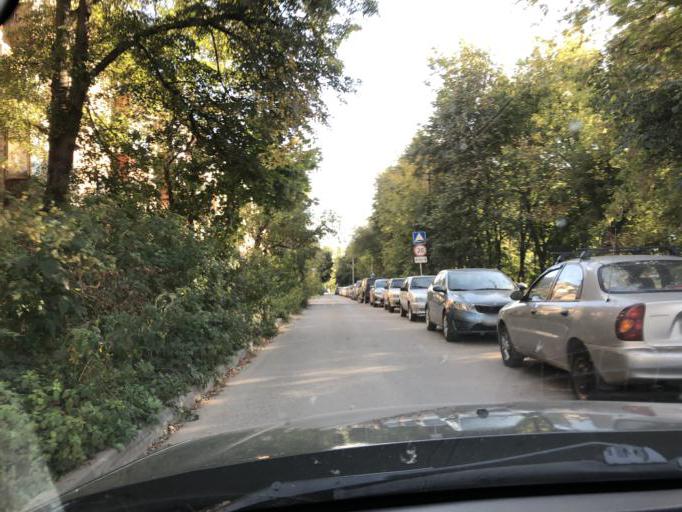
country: RU
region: Tula
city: Tula
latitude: 54.2104
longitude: 37.6074
